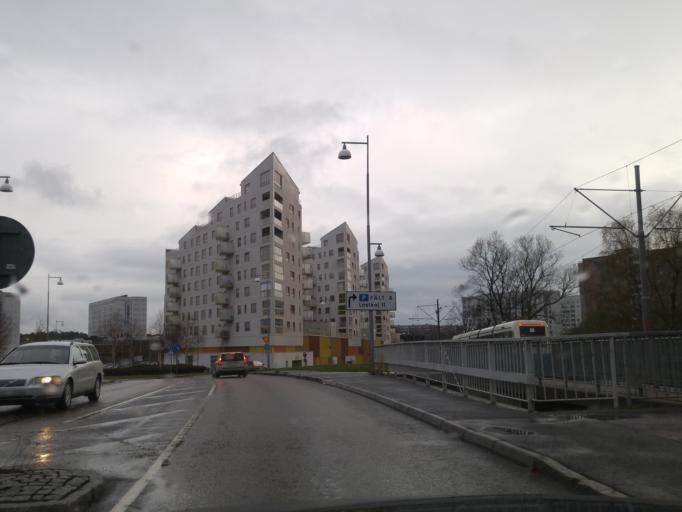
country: SE
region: Vaestra Goetaland
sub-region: Goteborg
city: Majorna
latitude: 57.6551
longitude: 11.9158
